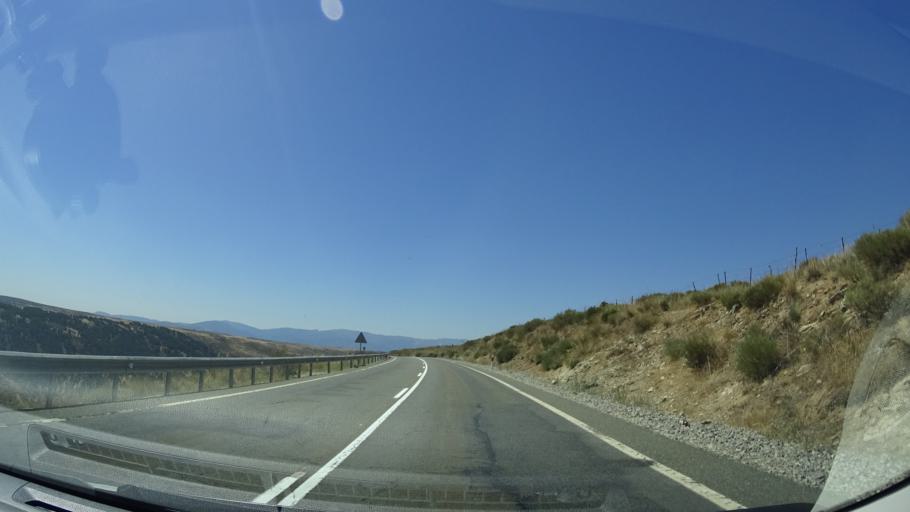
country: ES
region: Castille and Leon
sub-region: Provincia de Avila
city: Ojos-Albos
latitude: 40.6200
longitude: -4.5154
